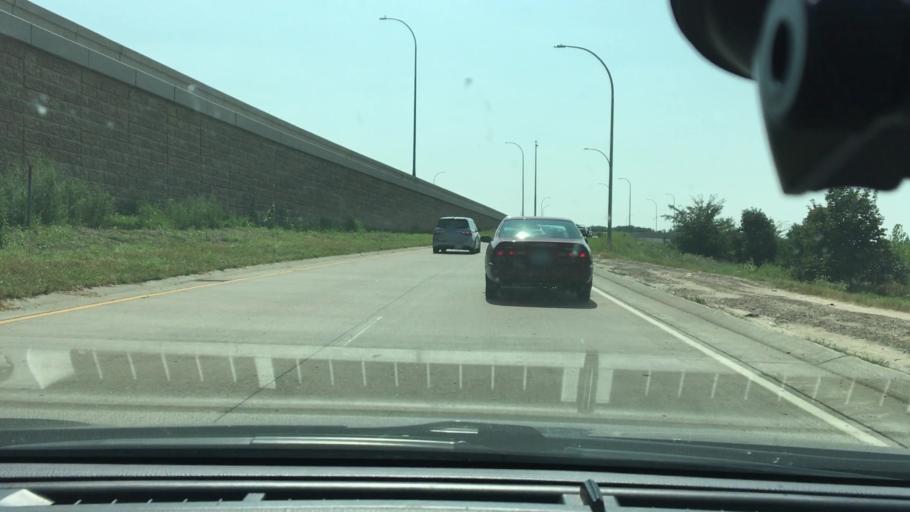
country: US
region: Minnesota
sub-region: Hennepin County
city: Osseo
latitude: 45.1079
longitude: -93.3925
